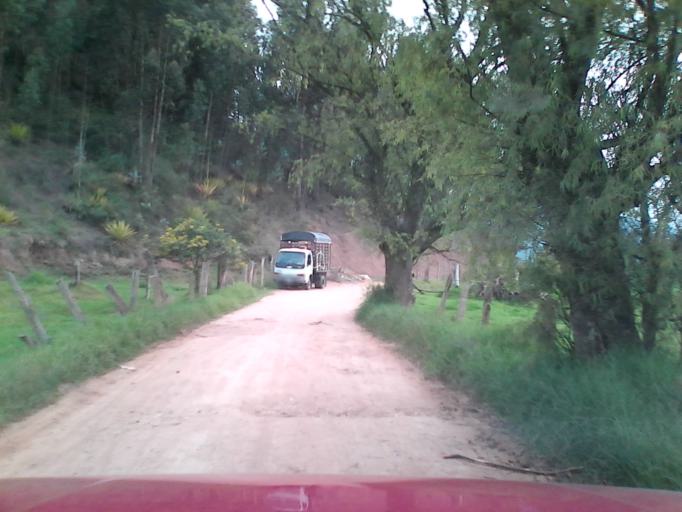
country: CO
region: Boyaca
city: Duitama
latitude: 5.8084
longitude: -72.9968
